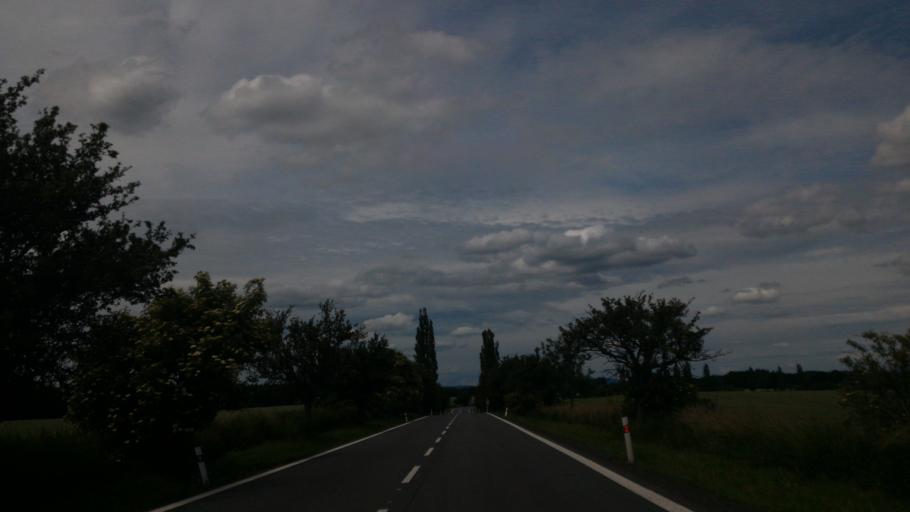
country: CZ
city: Duba
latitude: 50.5784
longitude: 14.5454
